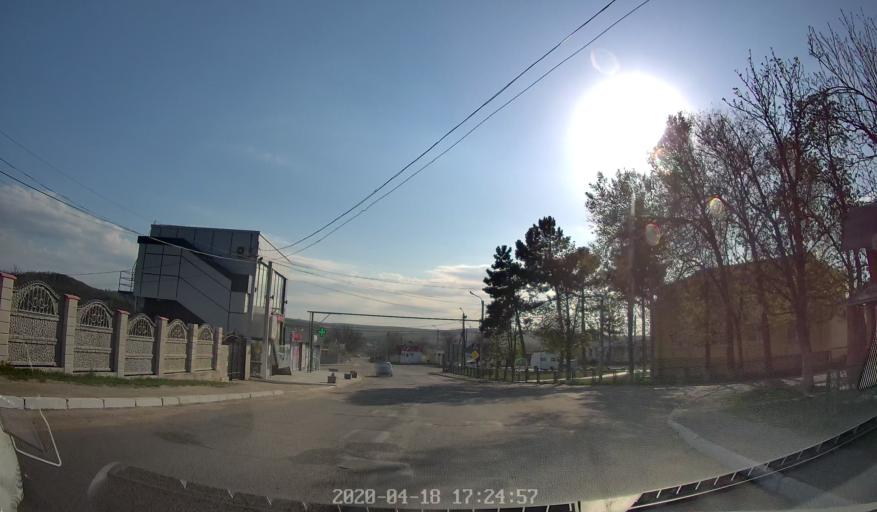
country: MD
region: Chisinau
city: Vadul lui Voda
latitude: 47.0646
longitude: 29.0099
